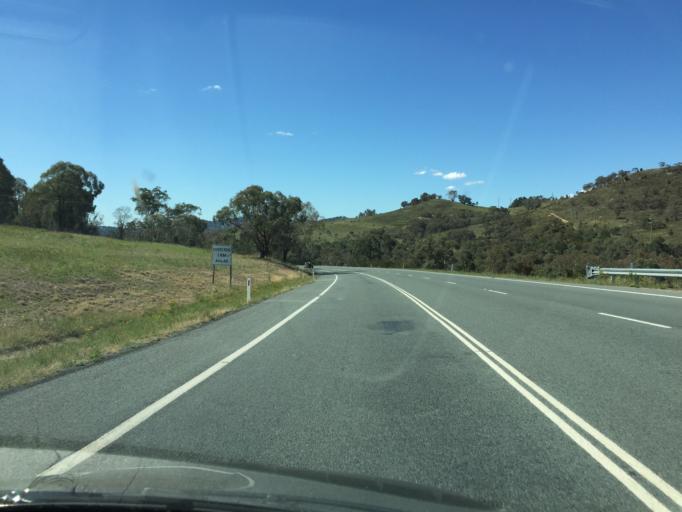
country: AU
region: Australian Capital Territory
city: Macarthur
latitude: -35.4462
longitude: 149.1307
